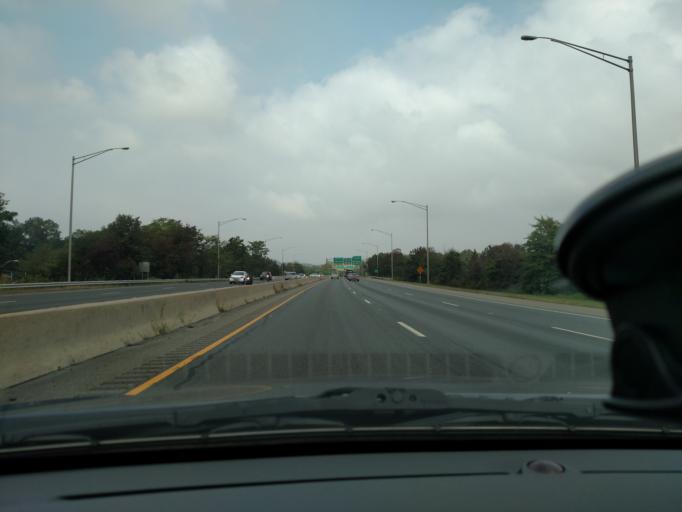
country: US
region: New Jersey
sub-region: Morris County
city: Morristown
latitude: 40.8048
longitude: -74.4442
